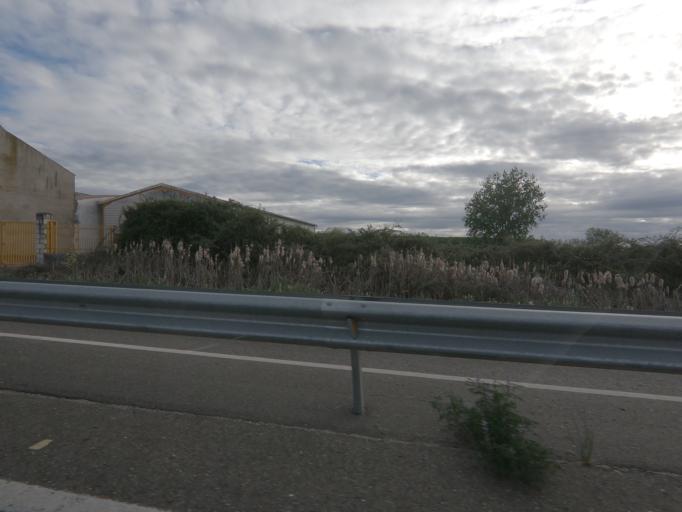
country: ES
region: Extremadura
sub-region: Provincia de Caceres
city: Coria
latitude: 39.9645
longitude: -6.5176
